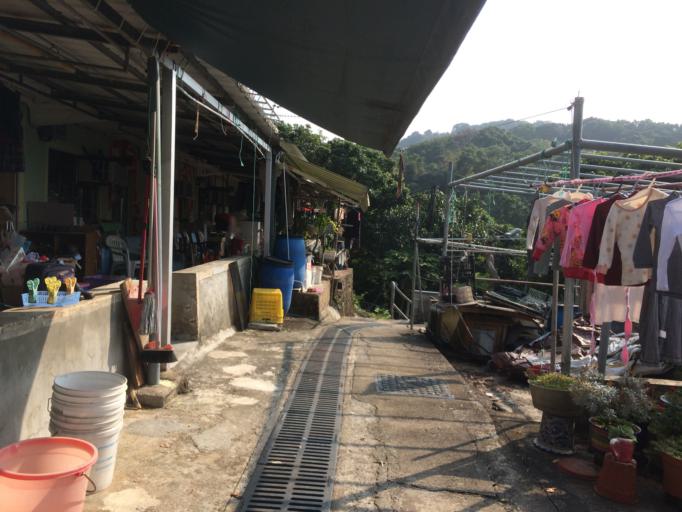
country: HK
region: Tai Po
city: Tai Po
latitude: 22.4552
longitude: 114.2145
